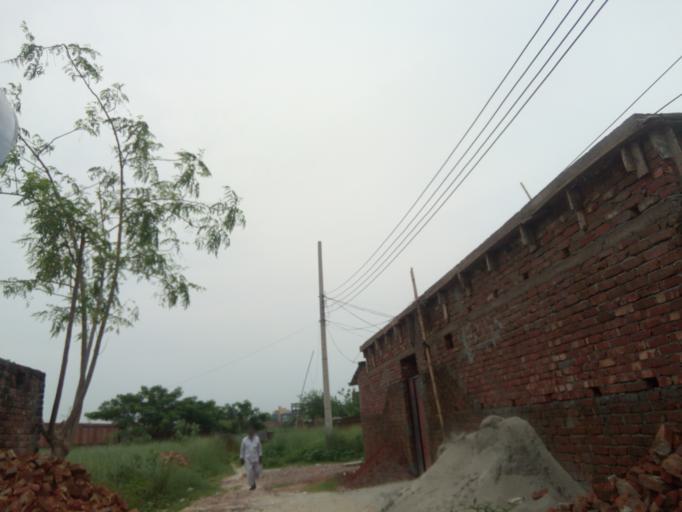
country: BD
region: Dhaka
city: Azimpur
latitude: 23.7453
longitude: 90.3553
